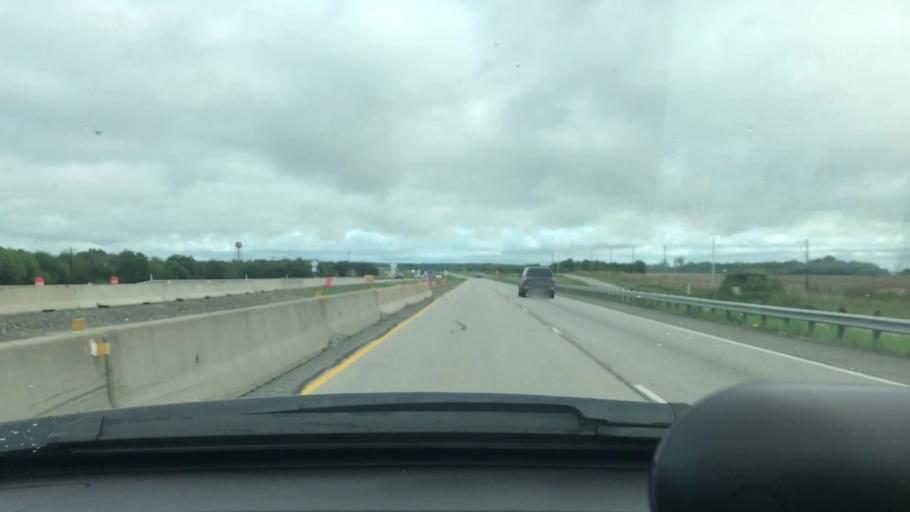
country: US
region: Texas
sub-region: Collin County
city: Anna
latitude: 33.3711
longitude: -96.5818
